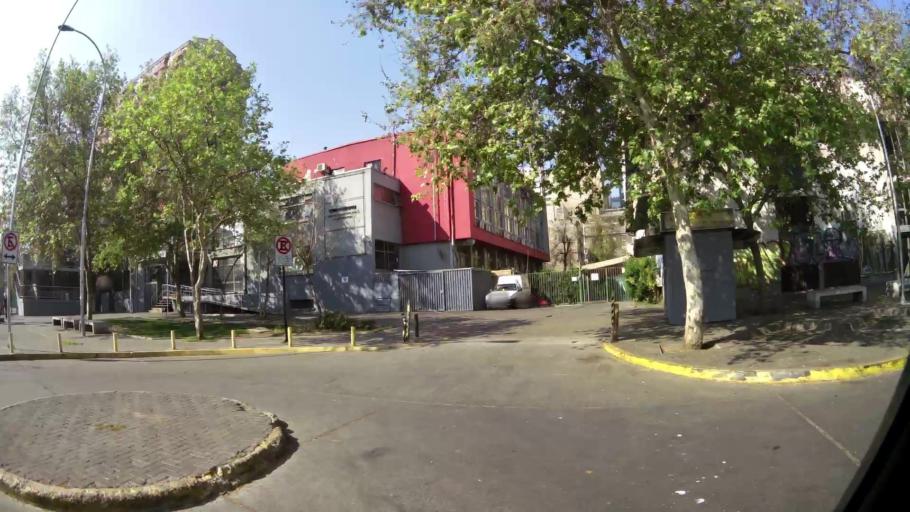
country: CL
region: Santiago Metropolitan
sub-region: Provincia de Santiago
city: Santiago
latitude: -33.4411
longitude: -70.6592
